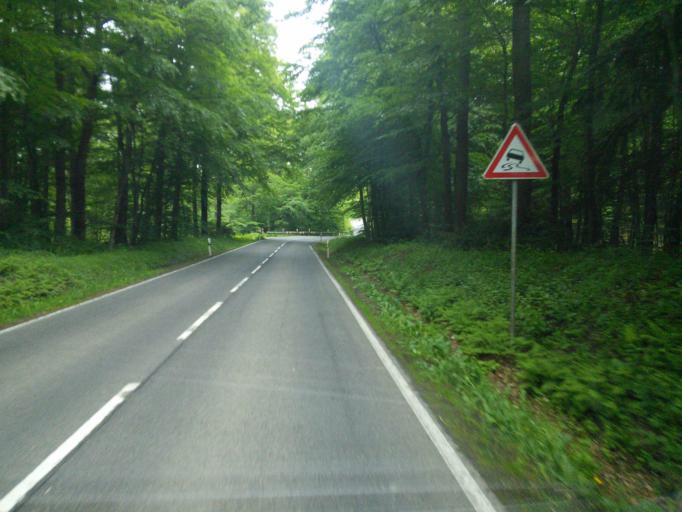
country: DE
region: Rheinland-Pfalz
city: Berg
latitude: 50.5719
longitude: 6.9118
